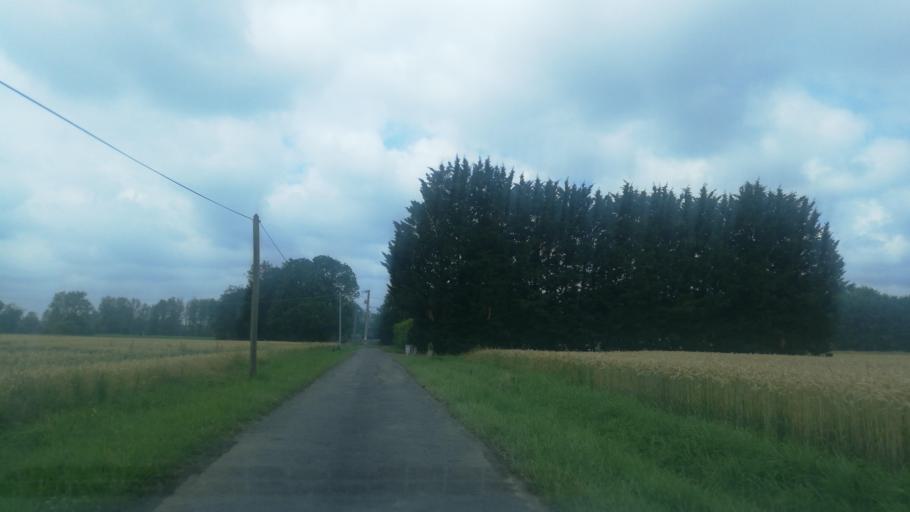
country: FR
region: Centre
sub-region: Departement du Loir-et-Cher
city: Saint-Romain-sur-Cher
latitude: 47.3370
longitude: 1.4490
